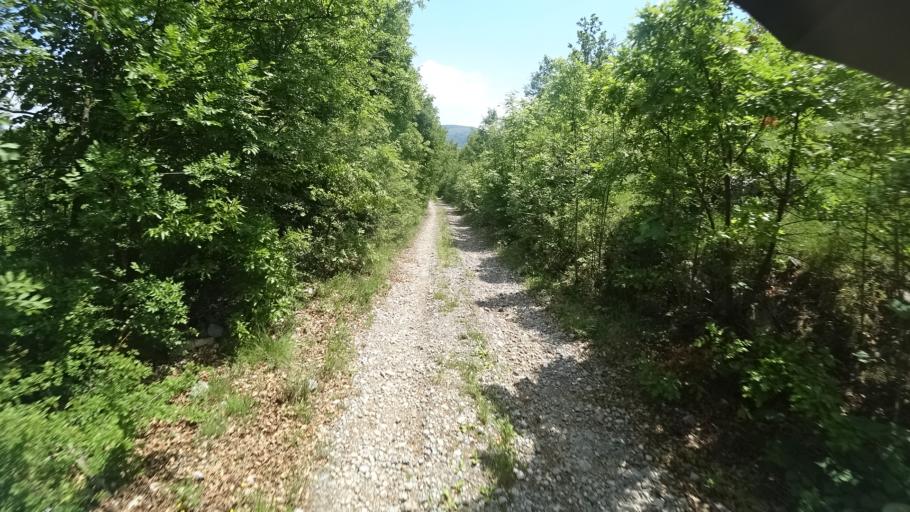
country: HR
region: Zadarska
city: Gracac
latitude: 44.4442
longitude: 15.9134
